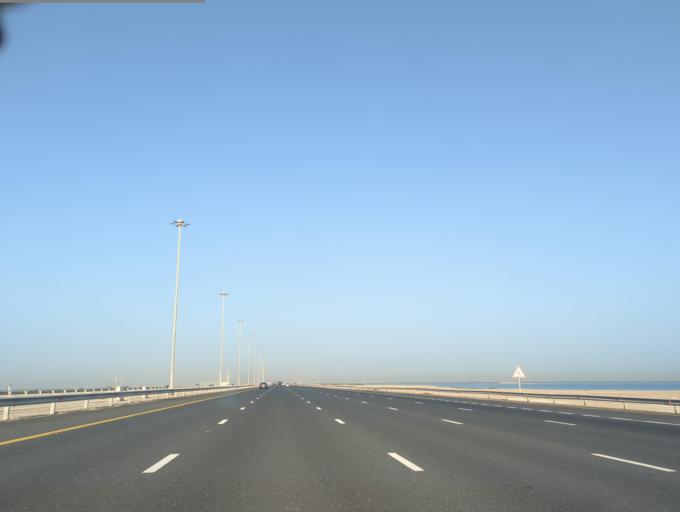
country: AE
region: Abu Dhabi
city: Abu Dhabi
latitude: 24.5115
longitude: 54.5491
